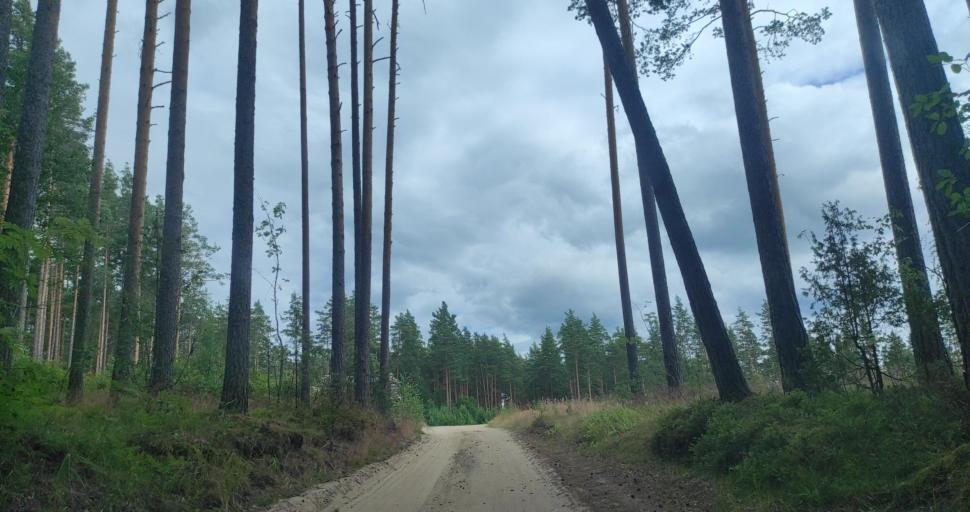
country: RU
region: Leningrad
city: Sapernoye
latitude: 60.6752
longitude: 29.9382
